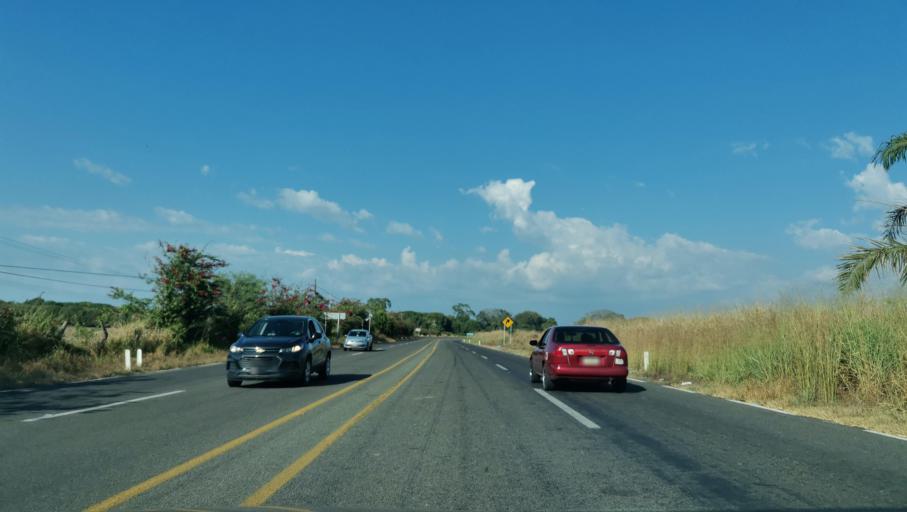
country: MX
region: Chiapas
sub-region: Tapachula
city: Congregacion Reforma
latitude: 14.8131
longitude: -92.3448
